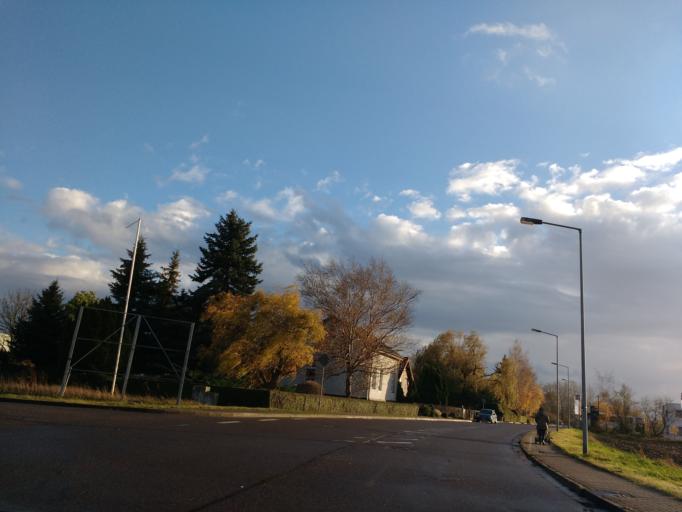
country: DE
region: Saxony-Anhalt
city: Peissen
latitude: 51.5080
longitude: 12.0535
